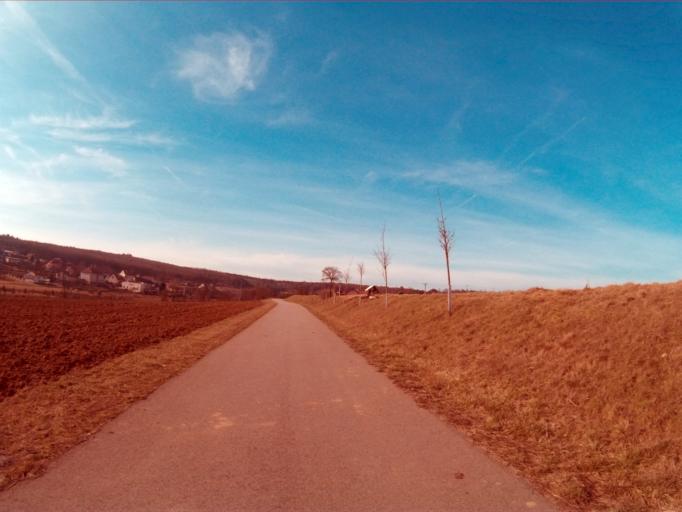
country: CZ
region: Vysocina
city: Mohelno
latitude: 49.1449
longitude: 16.1781
